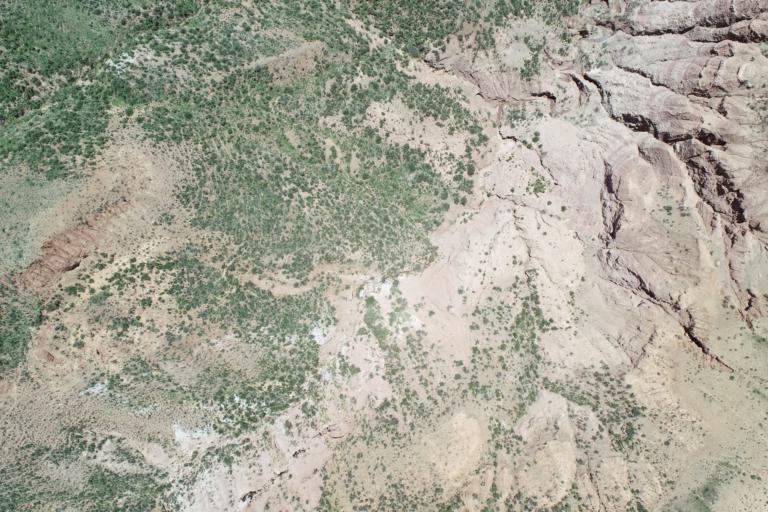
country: BO
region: La Paz
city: Curahuara de Carangas
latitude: -17.3104
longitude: -68.5057
